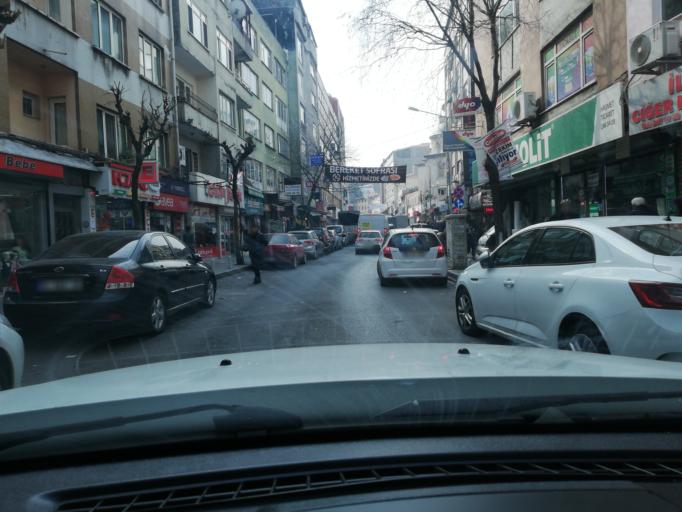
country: TR
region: Istanbul
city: Sisli
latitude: 41.0766
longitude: 28.9817
